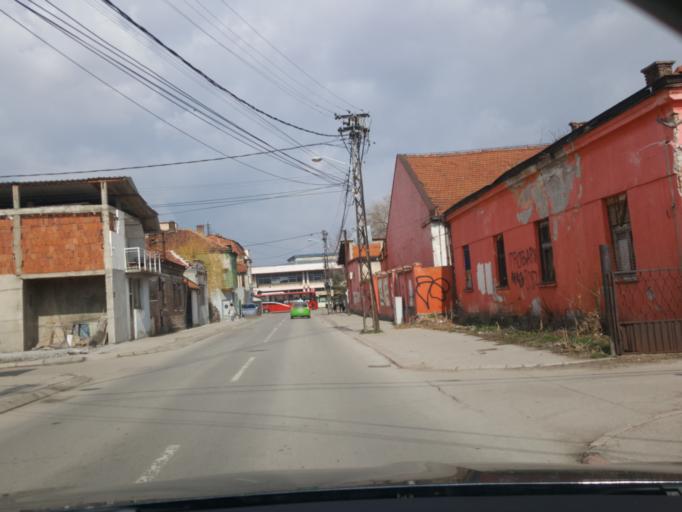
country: RS
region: Central Serbia
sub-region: Nisavski Okrug
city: Nis
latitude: 43.3144
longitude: 21.8771
